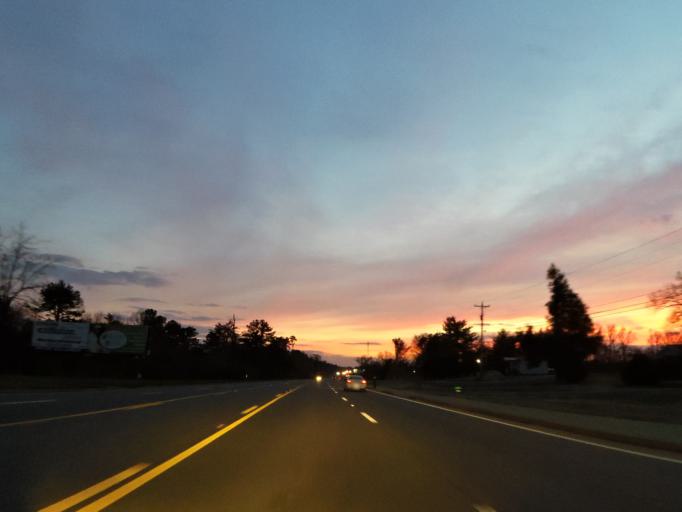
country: US
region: Tennessee
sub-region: Polk County
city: Benton
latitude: 35.1417
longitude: -84.7095
